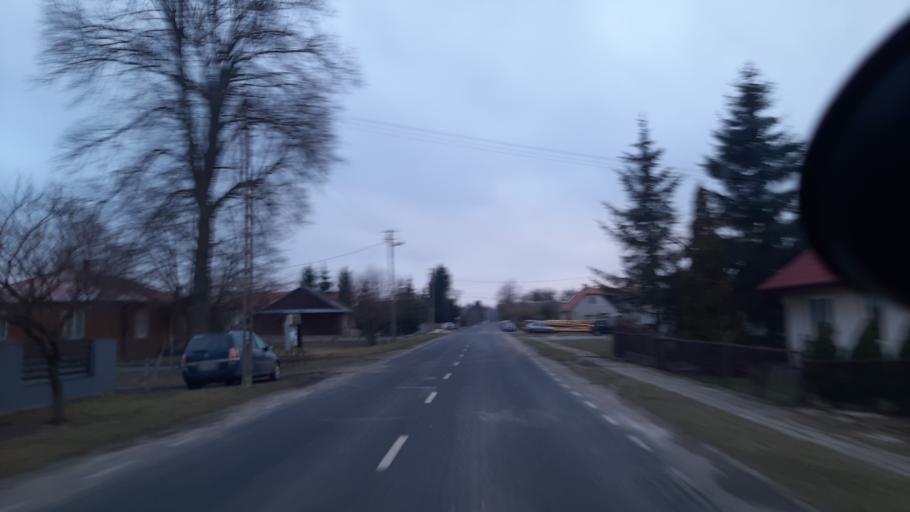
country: PL
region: Lublin Voivodeship
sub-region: Powiat parczewski
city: Debowa Kloda
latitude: 51.6376
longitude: 23.0423
